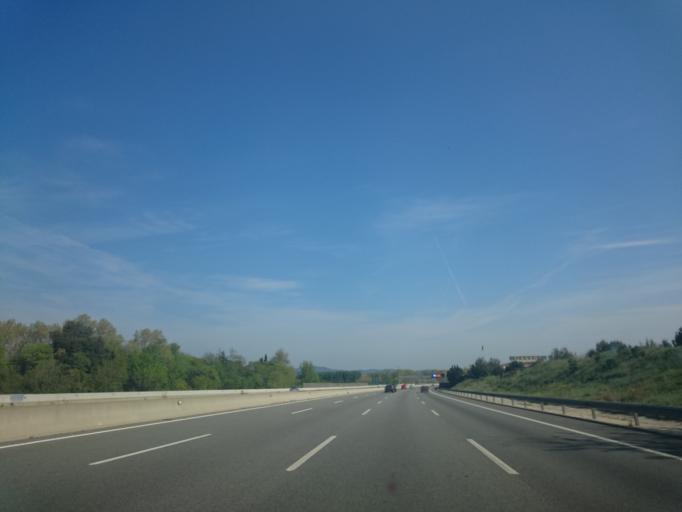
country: ES
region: Catalonia
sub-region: Provincia de Girona
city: Salt
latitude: 41.9723
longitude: 2.7784
